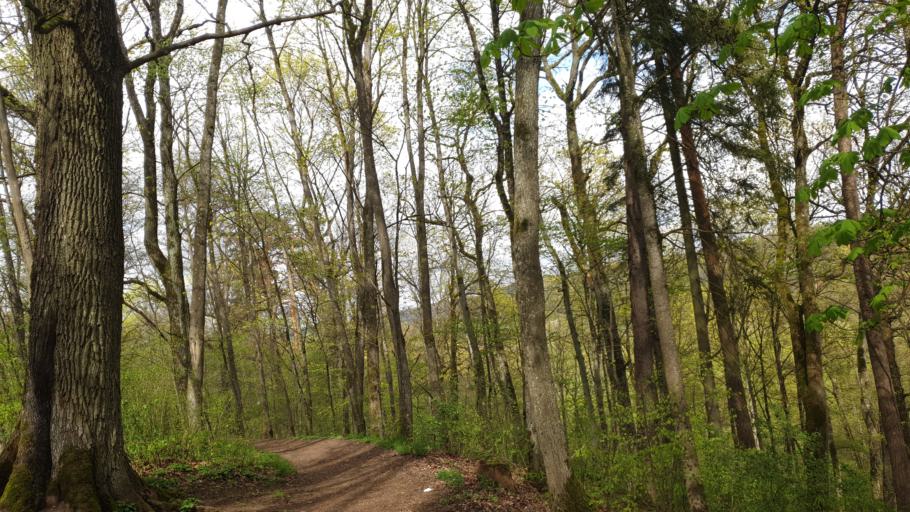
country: LT
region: Kauno apskritis
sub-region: Kauno rajonas
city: Akademija (Kaunas)
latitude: 54.9450
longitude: 23.7853
